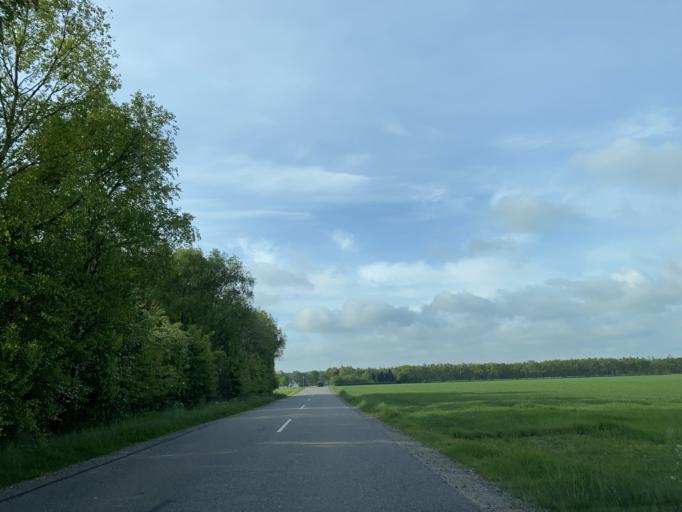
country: DK
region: Central Jutland
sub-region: Silkeborg Kommune
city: Svejbaek
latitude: 56.2257
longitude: 9.6818
